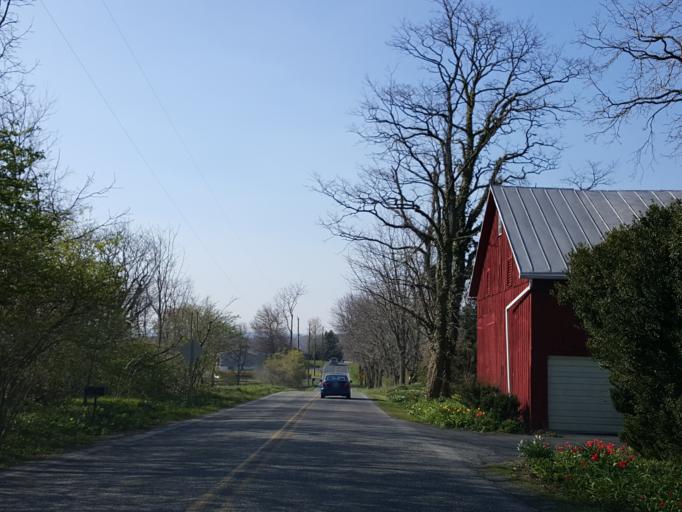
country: US
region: Pennsylvania
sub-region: Lebanon County
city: Annville
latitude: 40.3184
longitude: -76.5255
